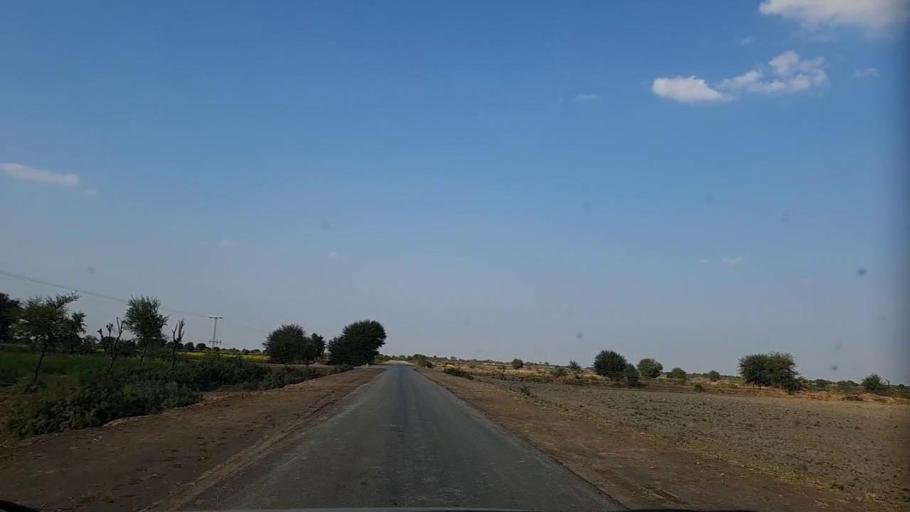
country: PK
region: Sindh
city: Pithoro
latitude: 25.6931
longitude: 69.2224
